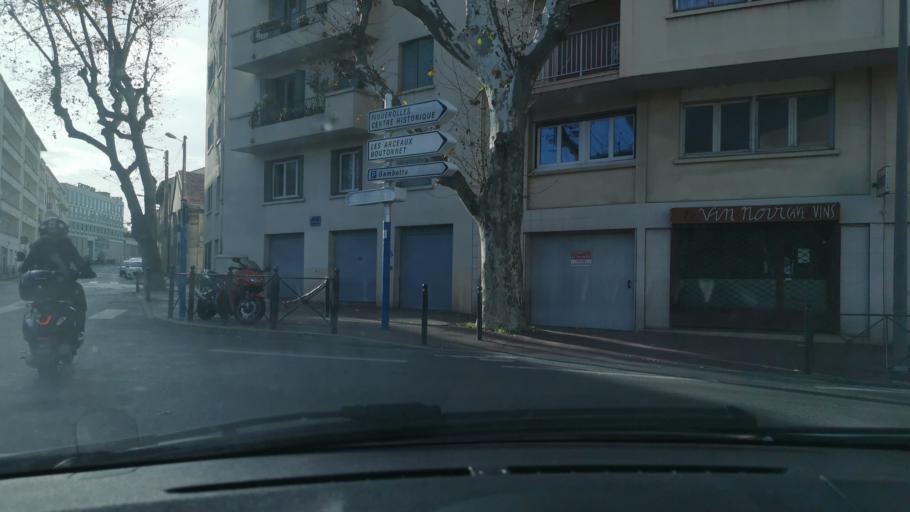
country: FR
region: Languedoc-Roussillon
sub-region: Departement de l'Herault
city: Montpellier
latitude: 43.6061
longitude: 3.8675
